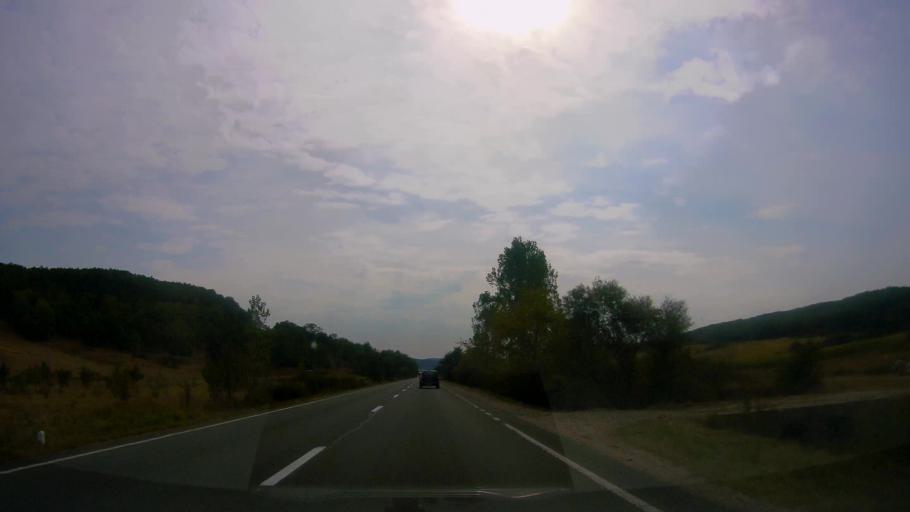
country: RO
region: Salaj
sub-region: Comuna Hida
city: Hida
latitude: 47.0522
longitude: 23.2369
